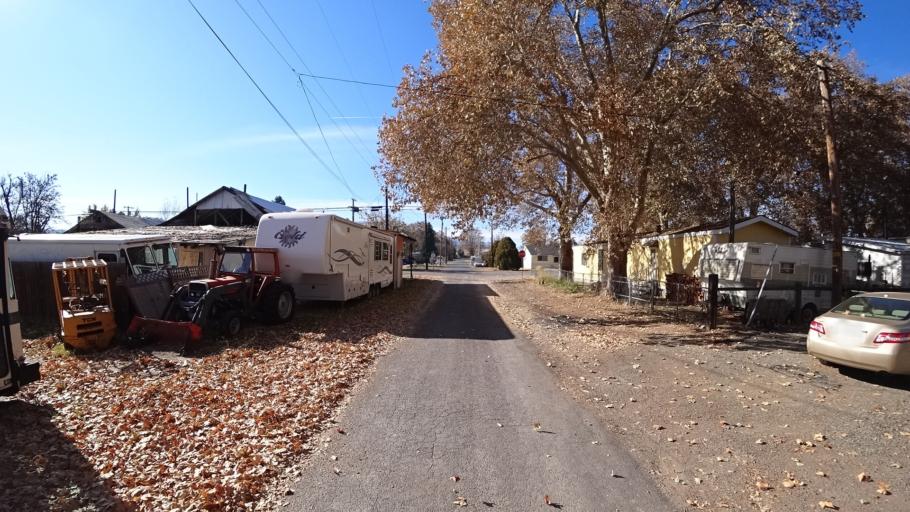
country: US
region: California
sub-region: Siskiyou County
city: Montague
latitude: 41.6448
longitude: -122.5218
